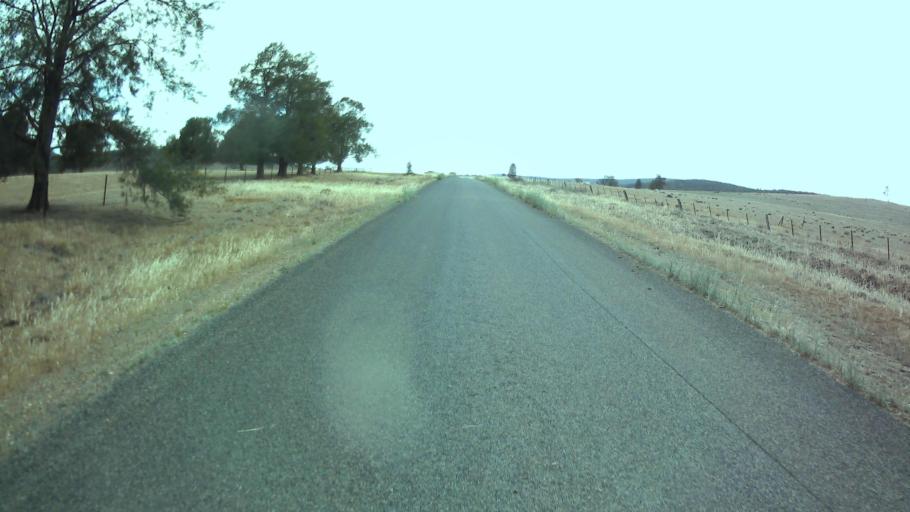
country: AU
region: New South Wales
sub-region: Weddin
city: Grenfell
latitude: -33.8447
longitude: 148.2512
